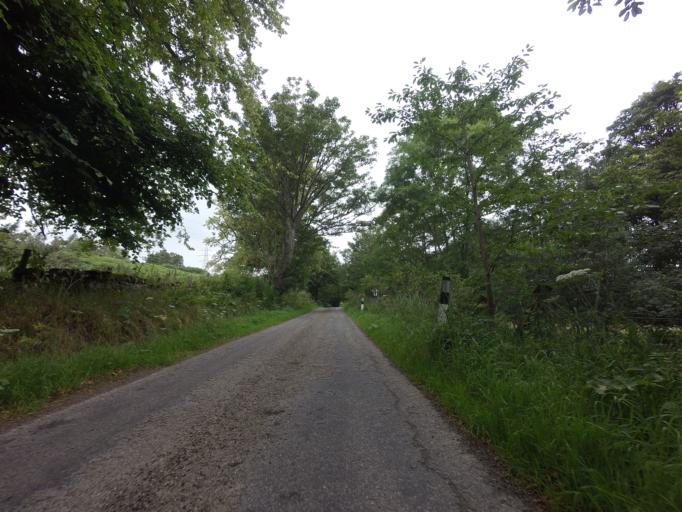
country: GB
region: Scotland
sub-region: Highland
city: Alness
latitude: 57.8931
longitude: -4.3749
